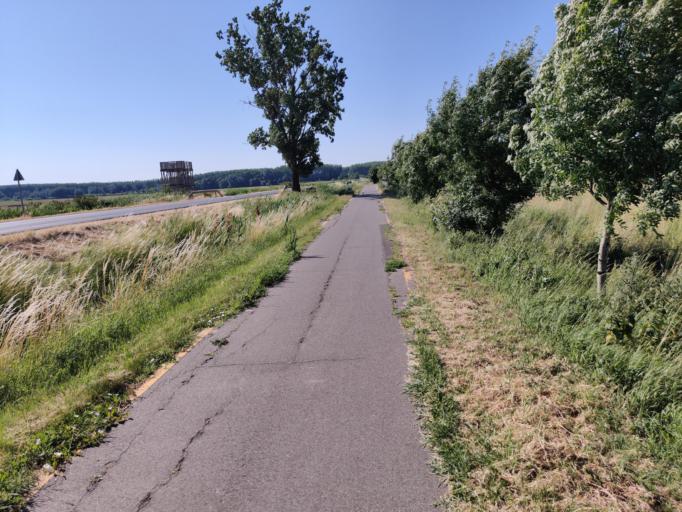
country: HU
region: Hajdu-Bihar
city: Balmazujvaros
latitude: 47.5912
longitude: 21.3425
